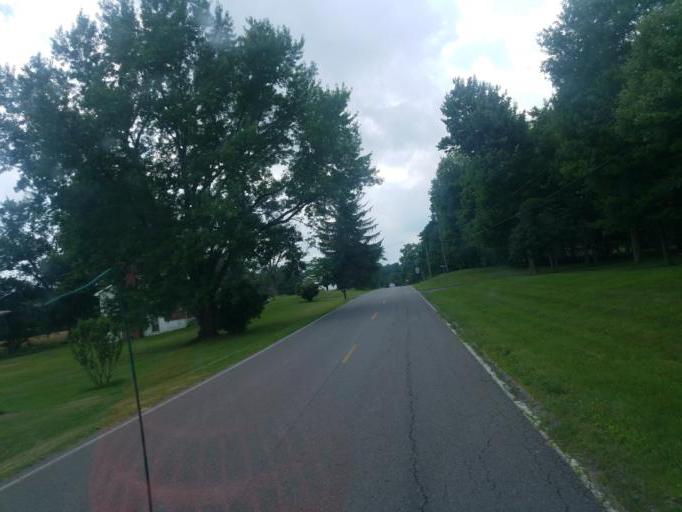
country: US
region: Ohio
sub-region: Columbiana County
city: Salem
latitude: 40.9731
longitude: -80.8533
